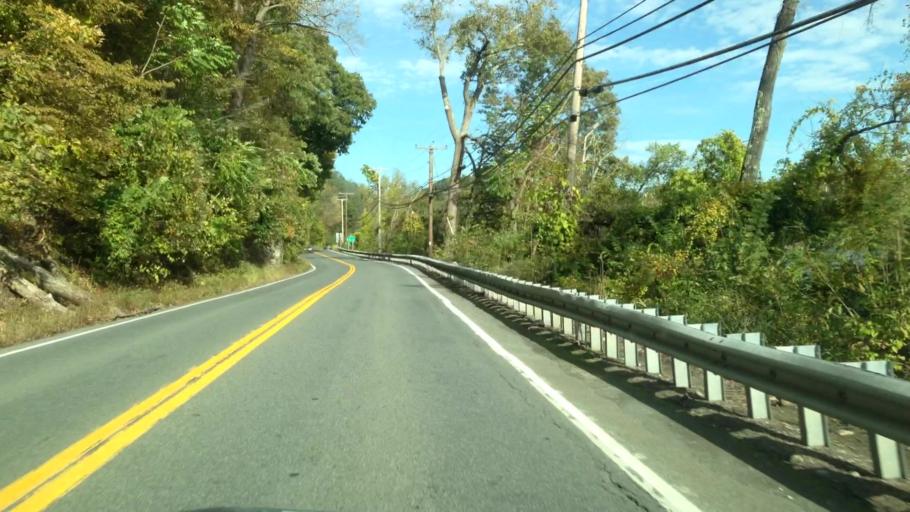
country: US
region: New York
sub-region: Ulster County
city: Kingston
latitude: 41.9022
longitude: -74.0144
